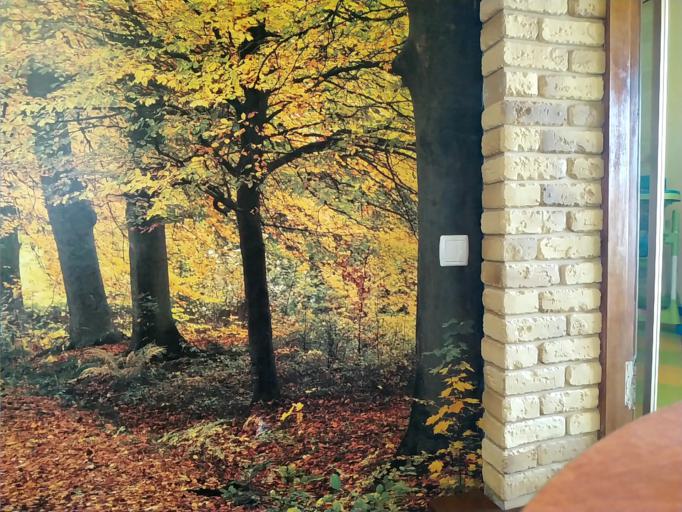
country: RU
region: Tverskaya
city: Maksatikha
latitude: 57.5764
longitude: 35.9389
